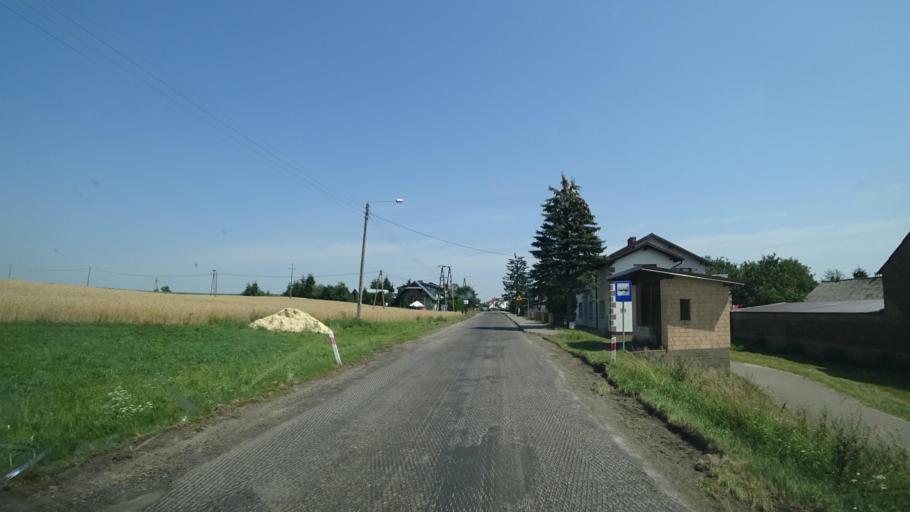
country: PL
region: Pomeranian Voivodeship
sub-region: Powiat chojnicki
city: Brusy
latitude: 53.8784
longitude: 17.6917
